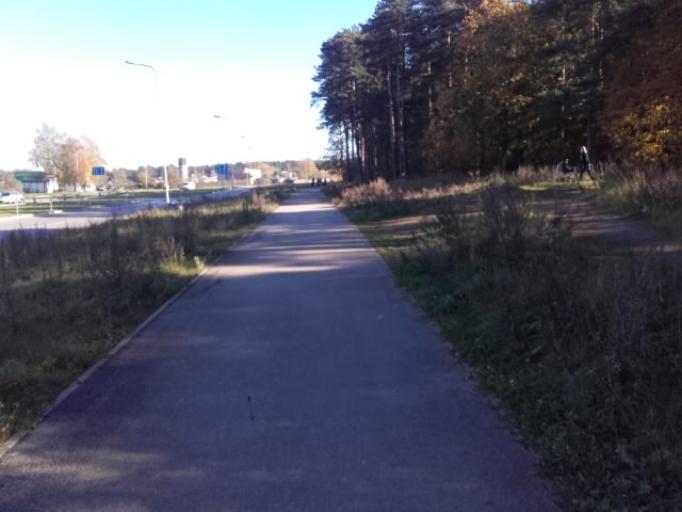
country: LV
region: Stopini
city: Ulbroka
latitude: 56.9376
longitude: 24.2160
